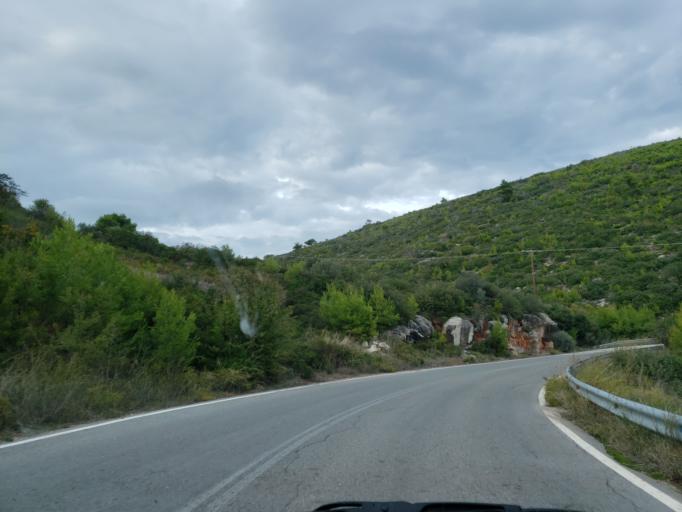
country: GR
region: Attica
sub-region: Nomarchia Anatolikis Attikis
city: Varnavas
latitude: 38.2133
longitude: 23.9416
